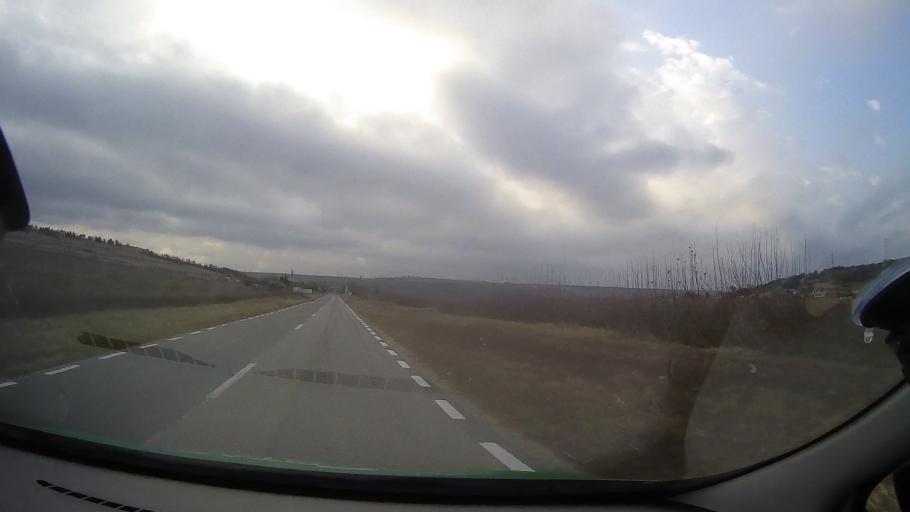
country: RO
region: Constanta
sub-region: Comuna Pestera
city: Pestera
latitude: 44.1965
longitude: 28.1310
